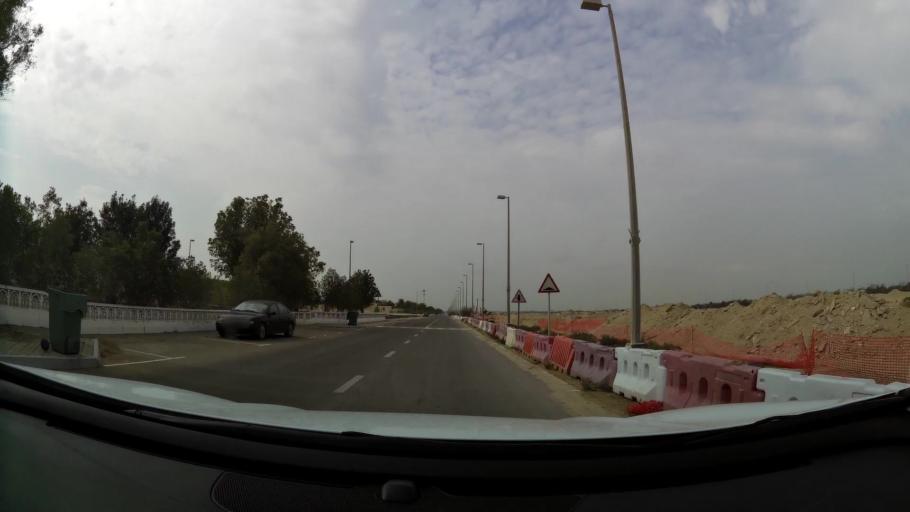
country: AE
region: Abu Dhabi
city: Abu Dhabi
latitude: 24.6466
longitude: 54.7267
